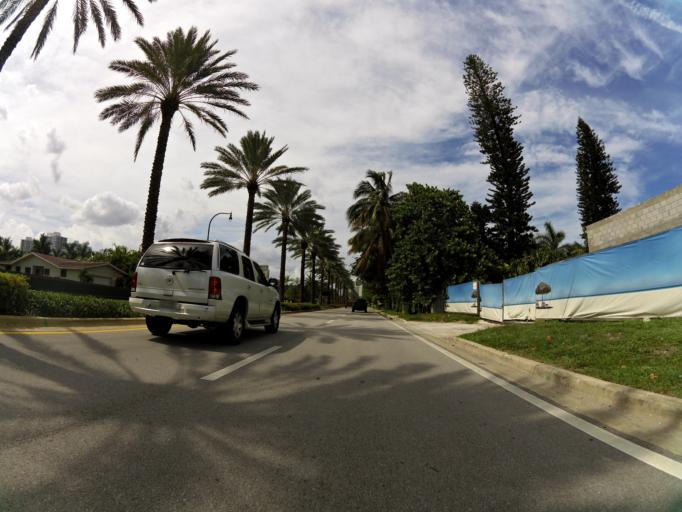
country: US
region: Florida
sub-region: Miami-Dade County
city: Sunny Isles Beach
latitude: 25.9674
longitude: -80.1195
